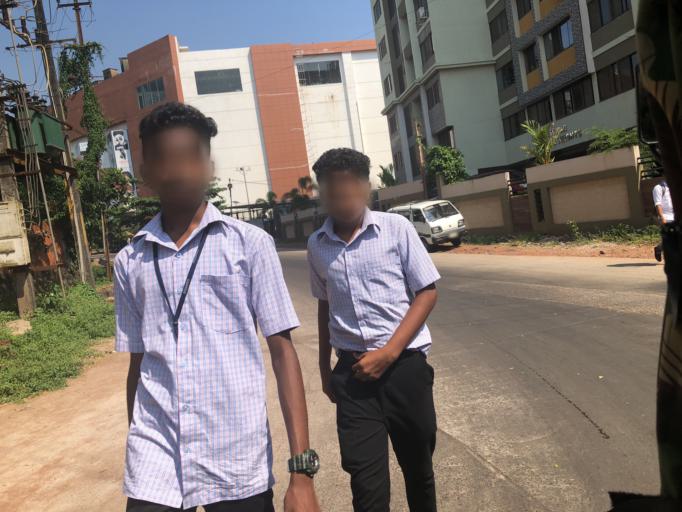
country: IN
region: Karnataka
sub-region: Dakshina Kannada
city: Ullal
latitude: 12.8573
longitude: 74.8370
